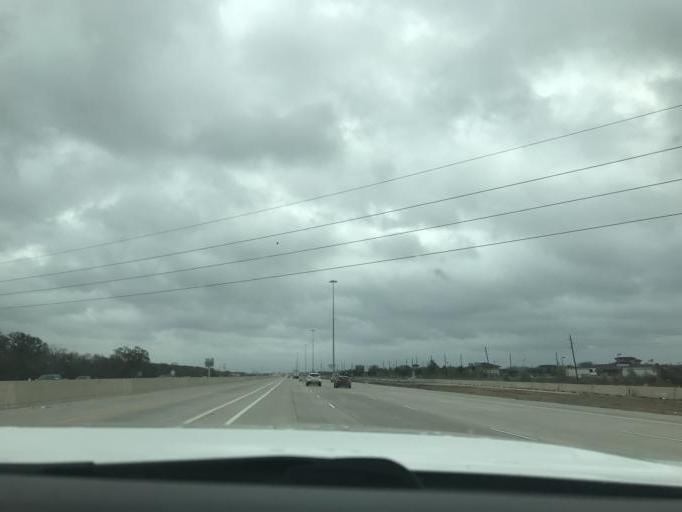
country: US
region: Texas
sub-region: Fort Bend County
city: Greatwood
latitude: 29.5575
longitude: -95.7091
